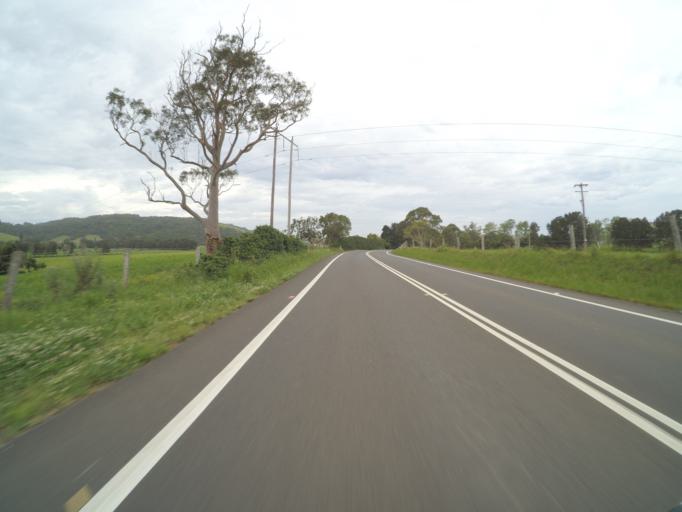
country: AU
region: New South Wales
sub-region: Kiama
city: Jamberoo
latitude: -34.6487
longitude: 150.7875
